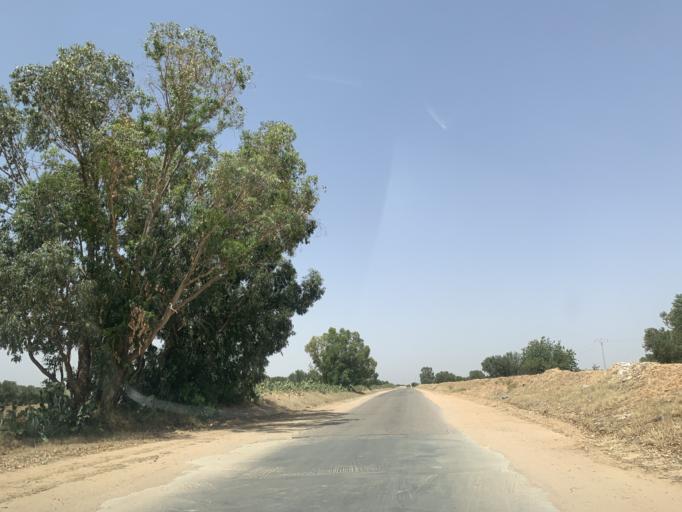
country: TN
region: Al Mahdiyah
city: Shurban
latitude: 35.1773
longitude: 10.2338
